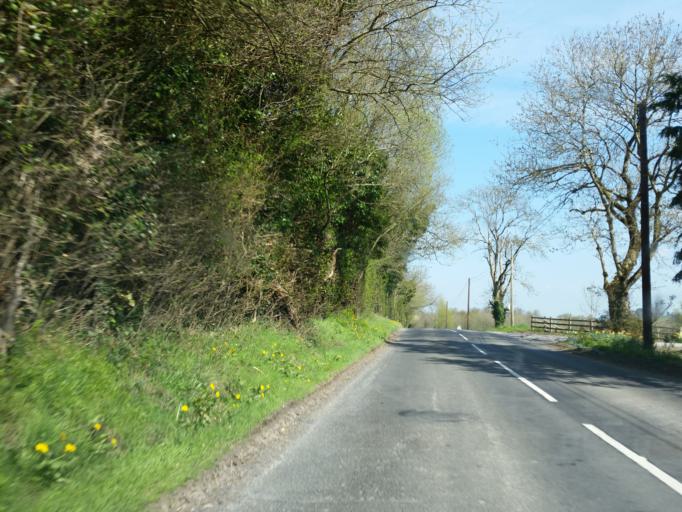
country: GB
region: Northern Ireland
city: Lisnaskea
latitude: 54.3016
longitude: -7.4161
